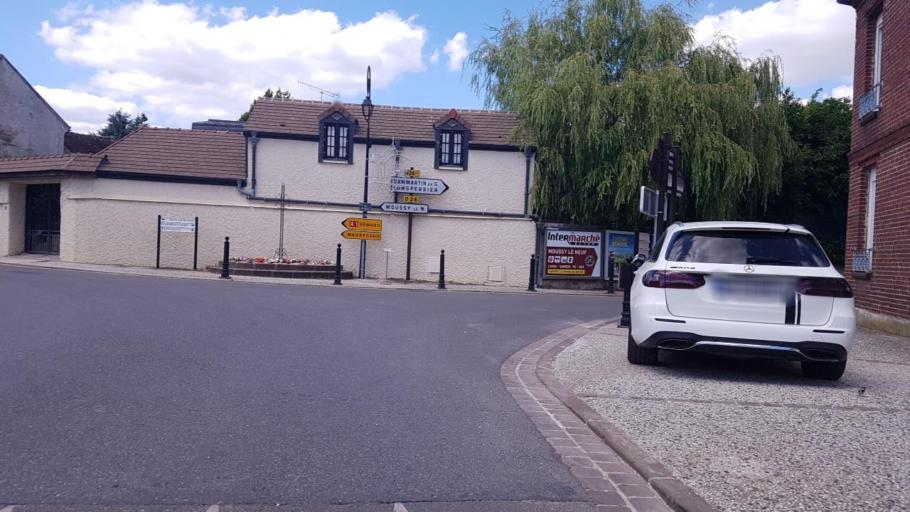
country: FR
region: Ile-de-France
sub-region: Departement de Seine-et-Marne
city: Moussy-le-Vieux
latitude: 49.0469
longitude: 2.6245
